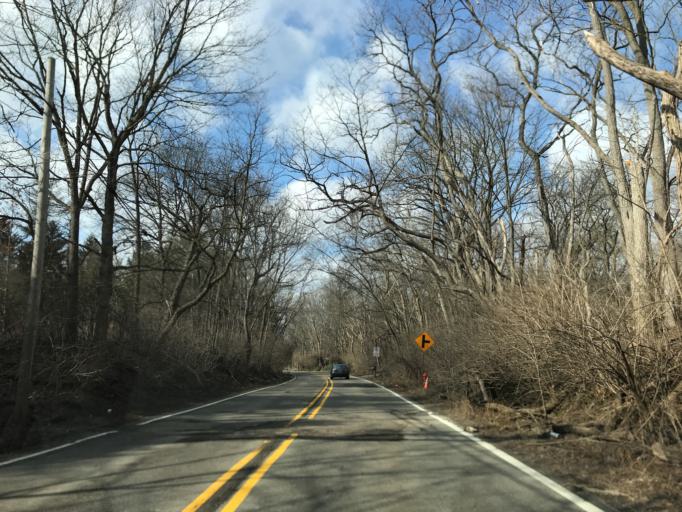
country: US
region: Michigan
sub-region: Washtenaw County
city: Ann Arbor
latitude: 42.2764
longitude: -83.6890
